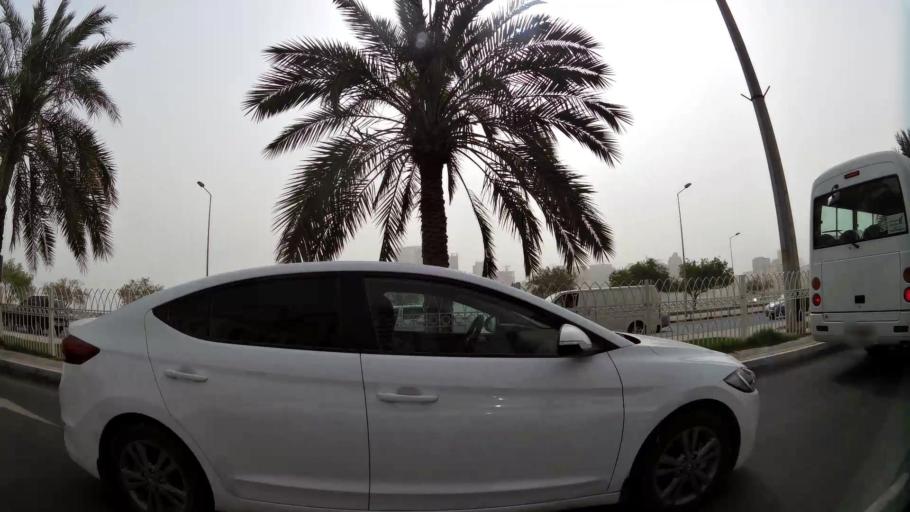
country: BH
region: Manama
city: Manama
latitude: 26.2254
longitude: 50.5983
